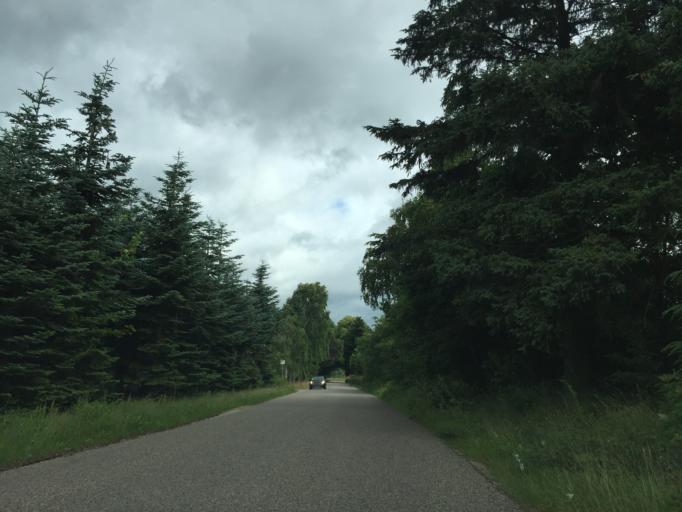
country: DK
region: Central Jutland
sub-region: Silkeborg Kommune
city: Svejbaek
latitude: 56.1660
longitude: 9.6548
